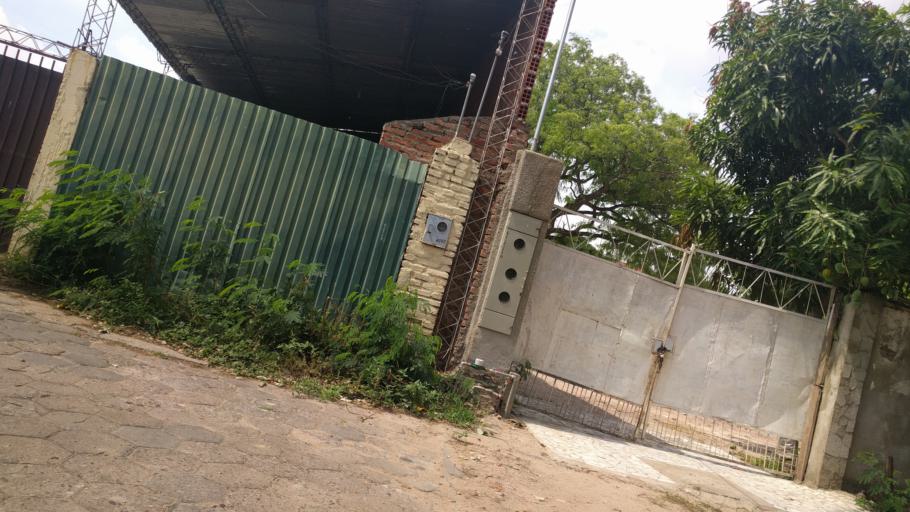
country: BO
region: Santa Cruz
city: Santa Cruz de la Sierra
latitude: -17.7889
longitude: -63.2180
